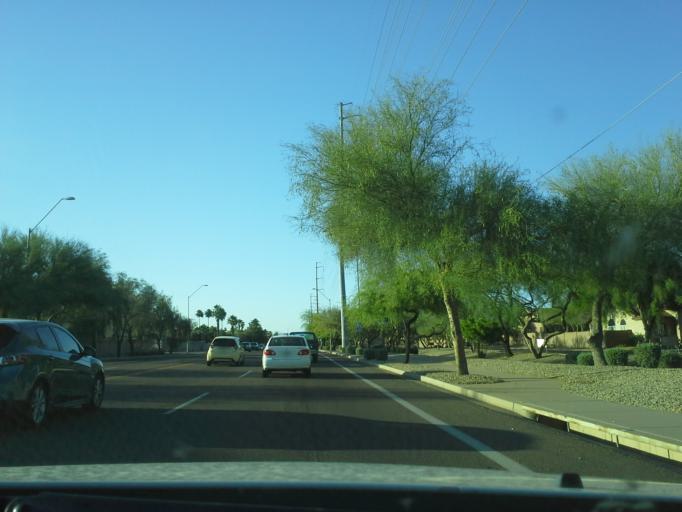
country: US
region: Arizona
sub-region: Maricopa County
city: Paradise Valley
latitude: 33.6626
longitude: -112.0136
